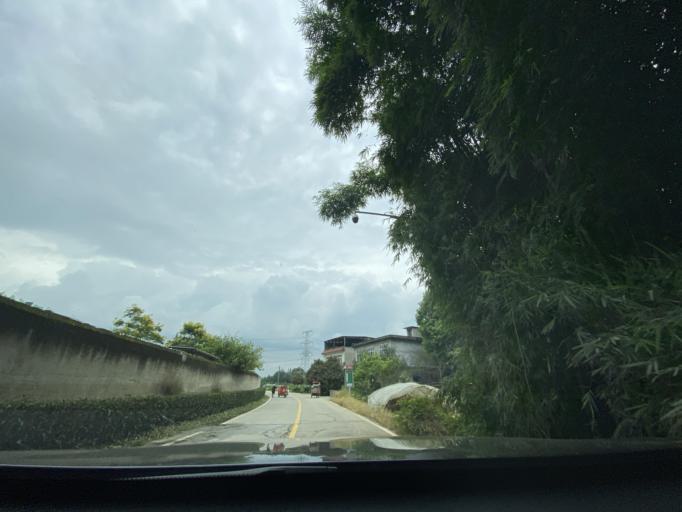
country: CN
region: Sichuan
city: Wujin
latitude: 30.3723
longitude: 103.9698
